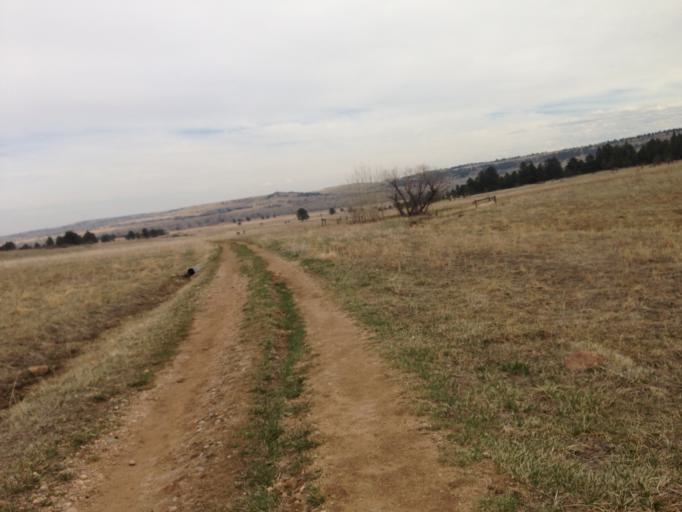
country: US
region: Colorado
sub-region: Boulder County
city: Boulder
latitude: 39.9545
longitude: -105.2635
